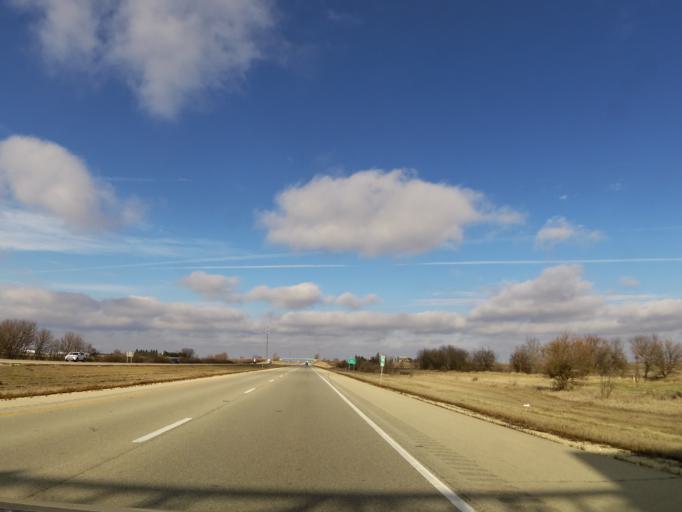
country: US
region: Illinois
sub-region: Ogle County
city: Rochelle
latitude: 41.8899
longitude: -89.0122
